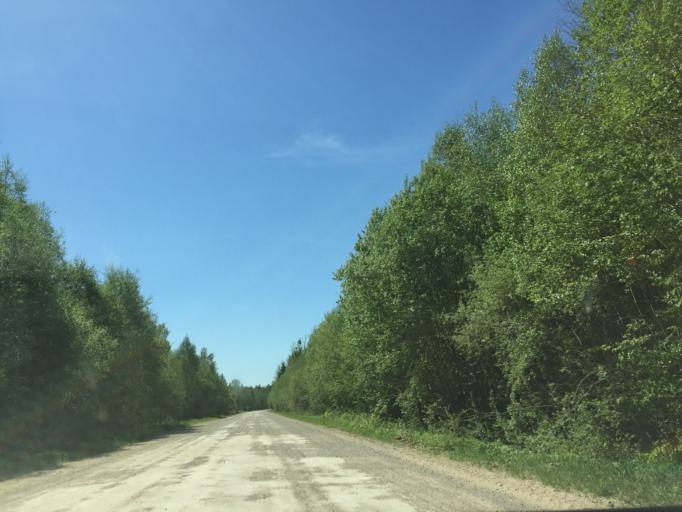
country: LV
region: Kegums
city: Kegums
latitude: 56.8724
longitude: 24.7765
